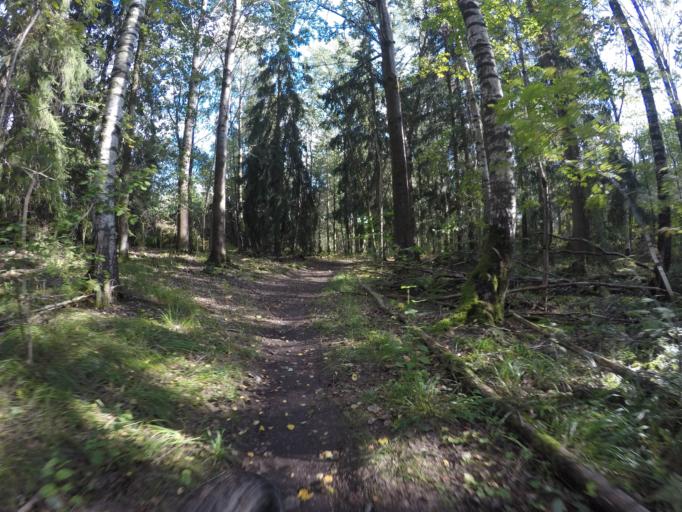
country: SE
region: Vaestmanland
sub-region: Kopings Kommun
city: Koping
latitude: 59.5081
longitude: 16.0281
